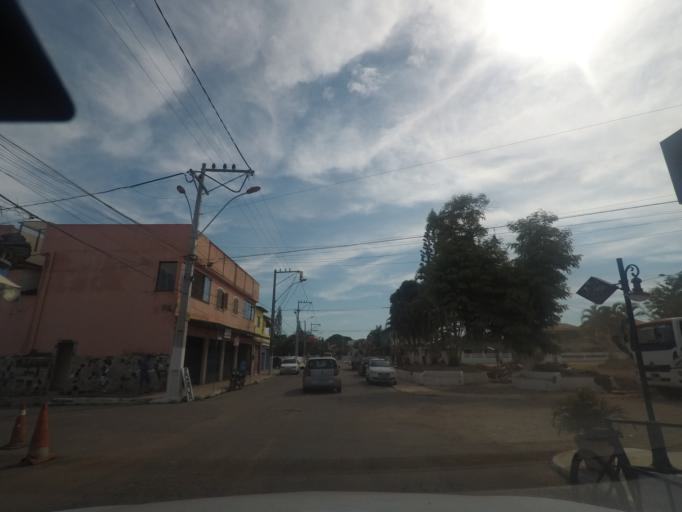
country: BR
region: Rio de Janeiro
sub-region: Marica
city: Marica
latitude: -22.9554
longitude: -42.8121
